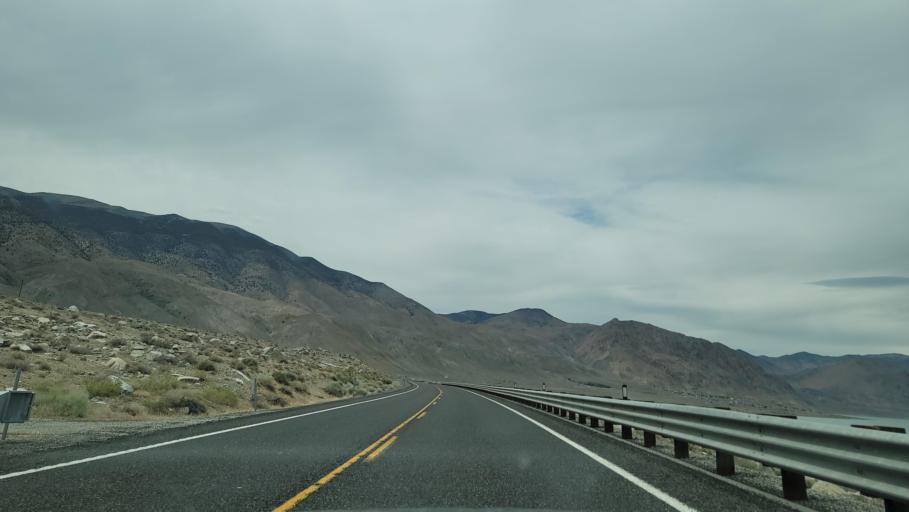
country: US
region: Nevada
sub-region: Mineral County
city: Hawthorne
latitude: 38.6123
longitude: -118.7198
